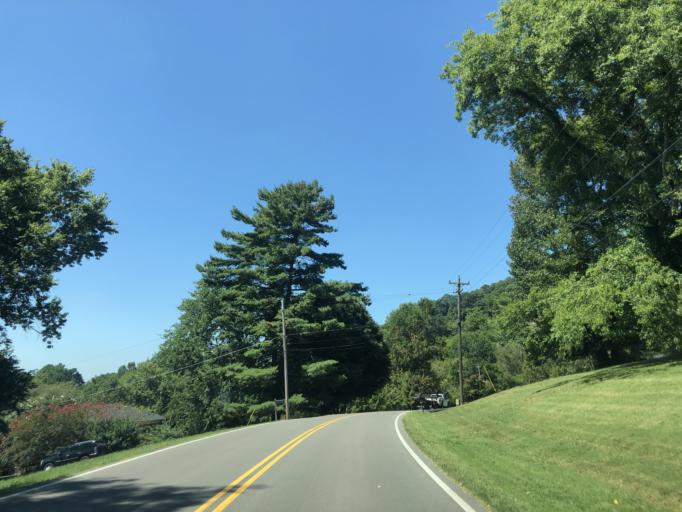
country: US
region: Tennessee
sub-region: Davidson County
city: Forest Hills
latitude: 36.0661
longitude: -86.8298
